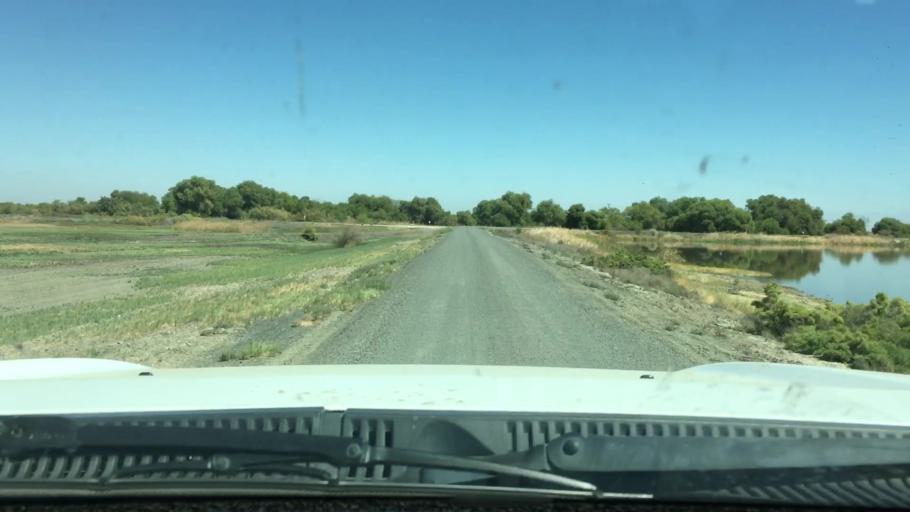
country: US
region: California
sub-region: Kern County
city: Lost Hills
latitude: 35.7489
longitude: -119.6005
